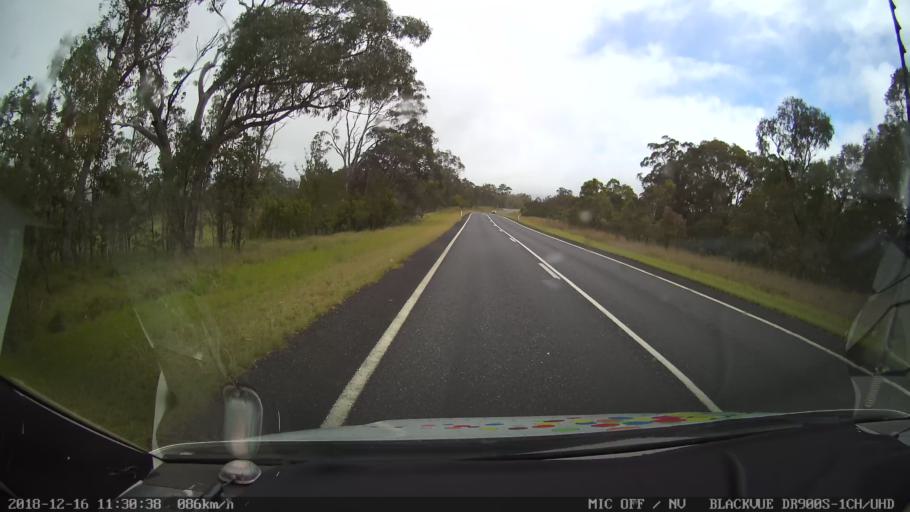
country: AU
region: New South Wales
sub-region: Tenterfield Municipality
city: Carrolls Creek
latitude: -29.0300
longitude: 152.1214
